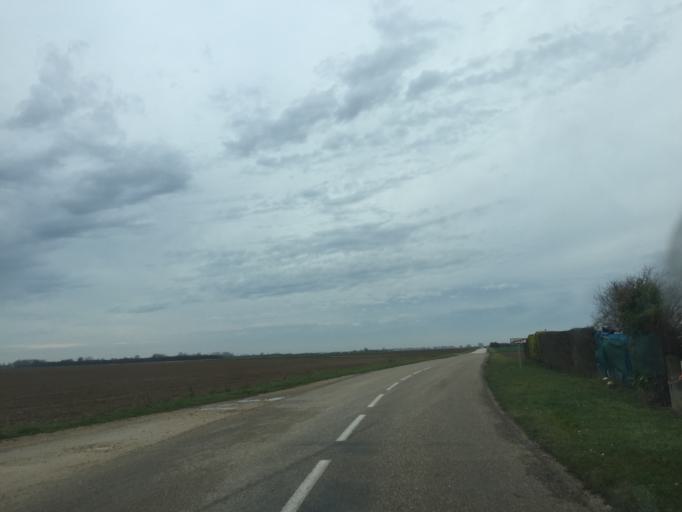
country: FR
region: Franche-Comte
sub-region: Departement du Jura
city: Tavaux
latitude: 47.0351
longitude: 5.4357
